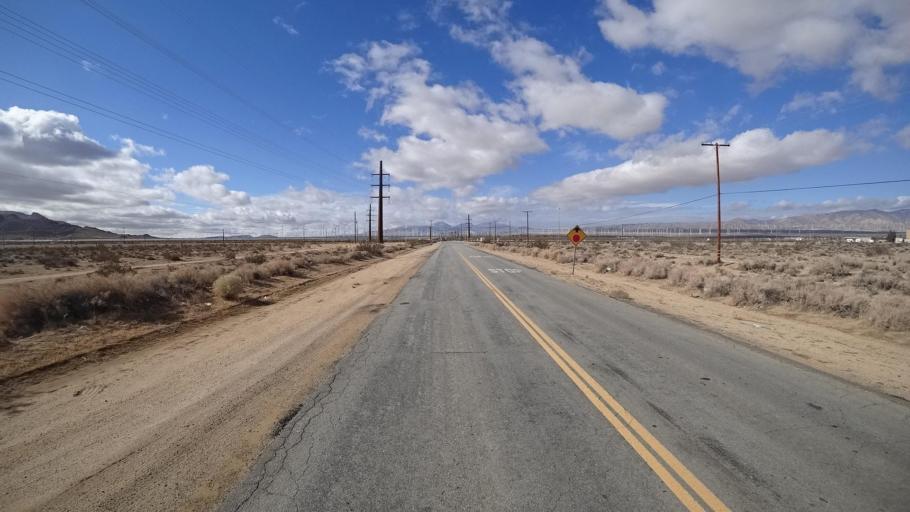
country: US
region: California
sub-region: Kern County
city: Mojave
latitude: 35.0247
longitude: -118.1625
